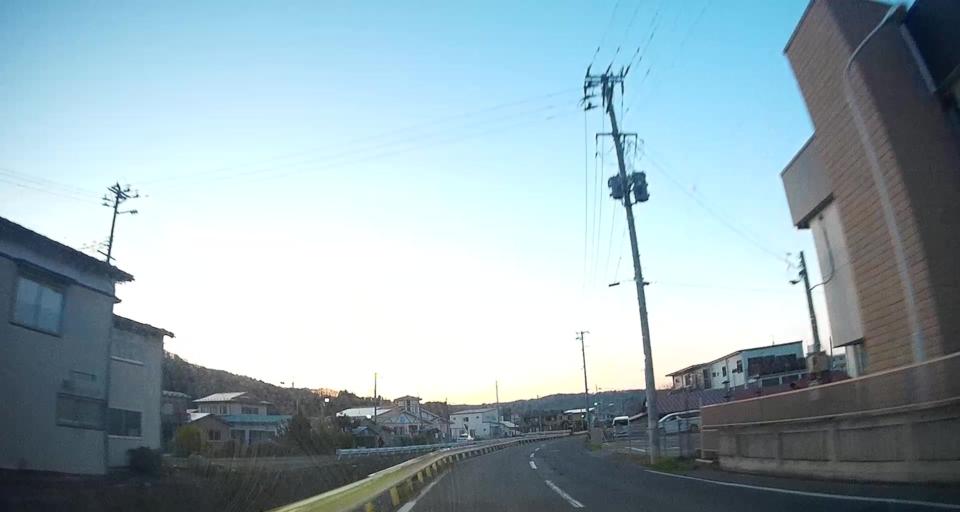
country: JP
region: Aomori
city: Hachinohe
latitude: 40.1830
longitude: 141.7725
